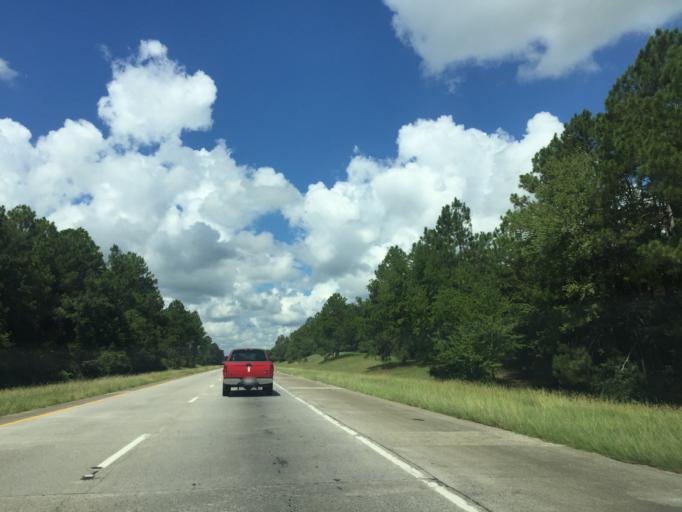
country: US
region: Georgia
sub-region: Candler County
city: Metter
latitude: 32.3799
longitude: -82.1973
